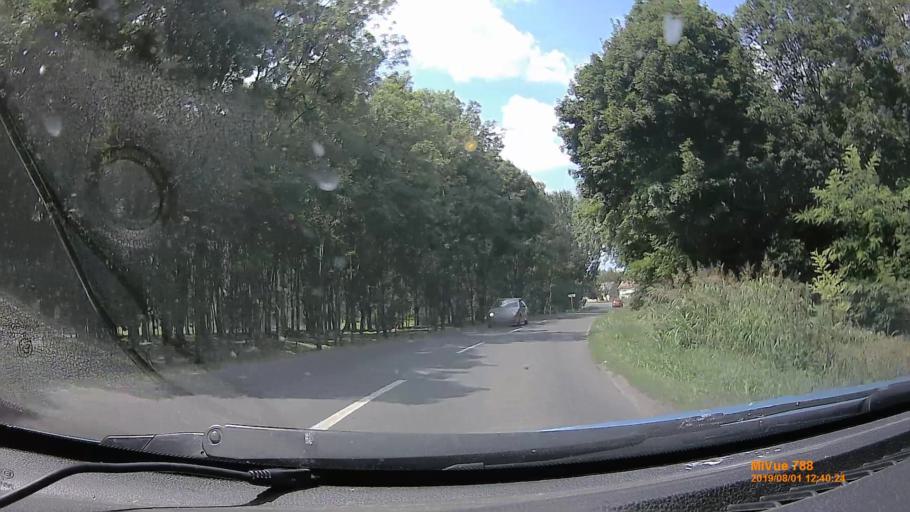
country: HU
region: Baranya
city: Harkany
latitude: 45.8352
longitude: 18.1855
